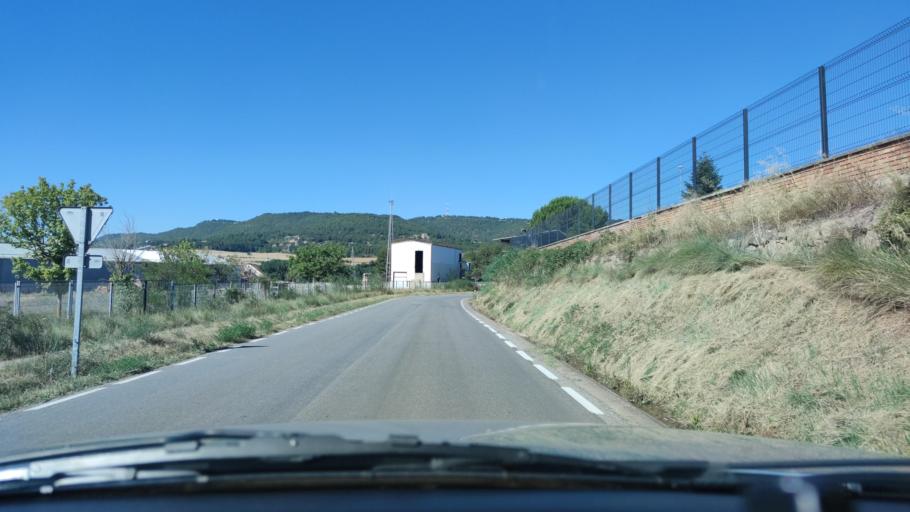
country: ES
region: Catalonia
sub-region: Provincia de Lleida
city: Solsona
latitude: 41.9888
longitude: 1.5098
